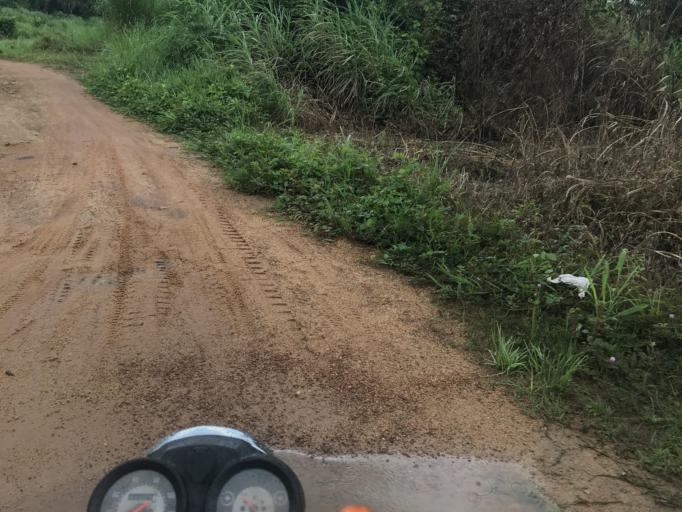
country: GN
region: Nzerekore
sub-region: Prefecture de Guekedou
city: Gueckedou
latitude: 8.4735
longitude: -10.2858
